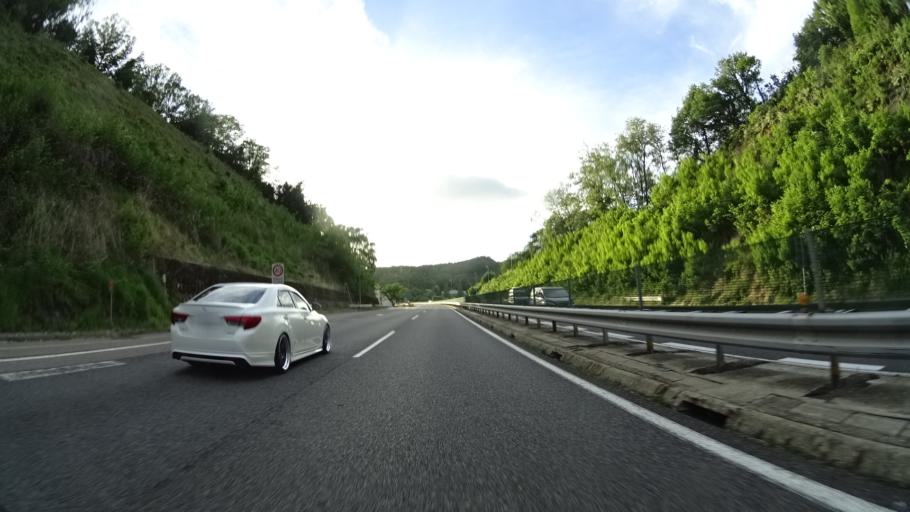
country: JP
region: Gifu
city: Mizunami
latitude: 35.3702
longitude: 137.2407
